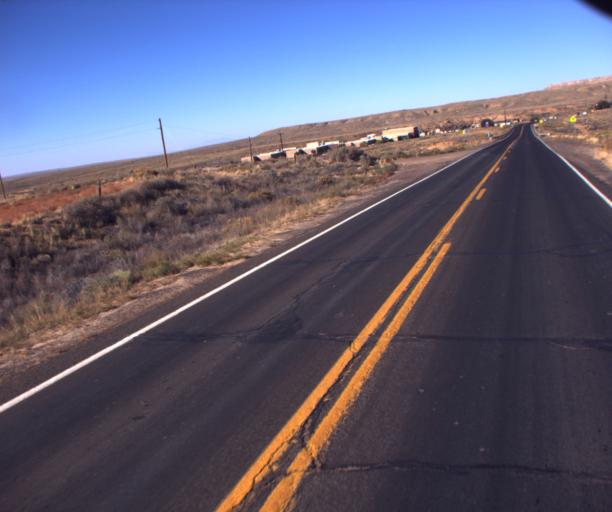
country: US
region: Arizona
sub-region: Navajo County
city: First Mesa
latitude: 35.7929
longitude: -110.4995
